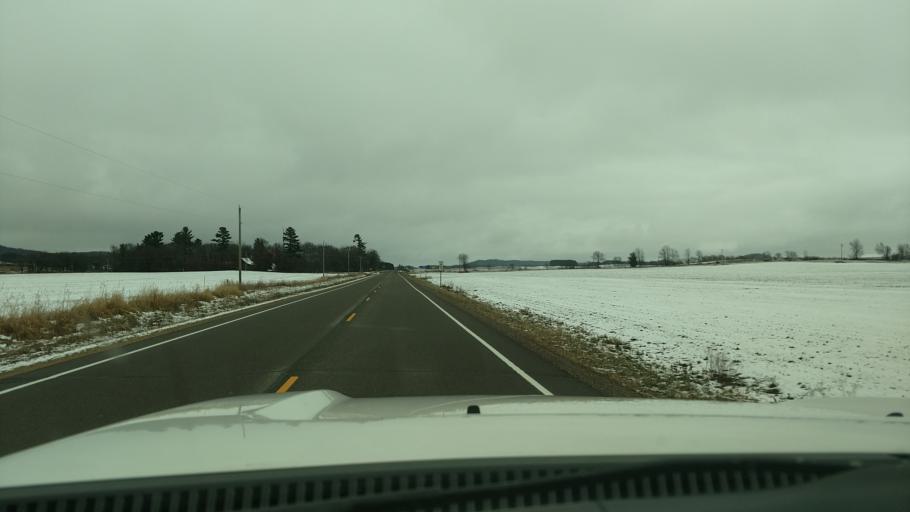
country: US
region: Wisconsin
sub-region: Dunn County
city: Colfax
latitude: 45.1427
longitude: -91.6922
